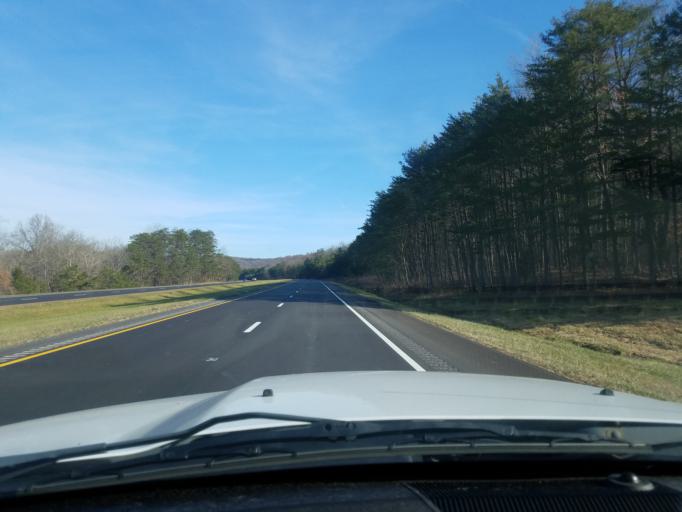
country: US
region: Ohio
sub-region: Adams County
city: Peebles
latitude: 38.9925
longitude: -83.3077
